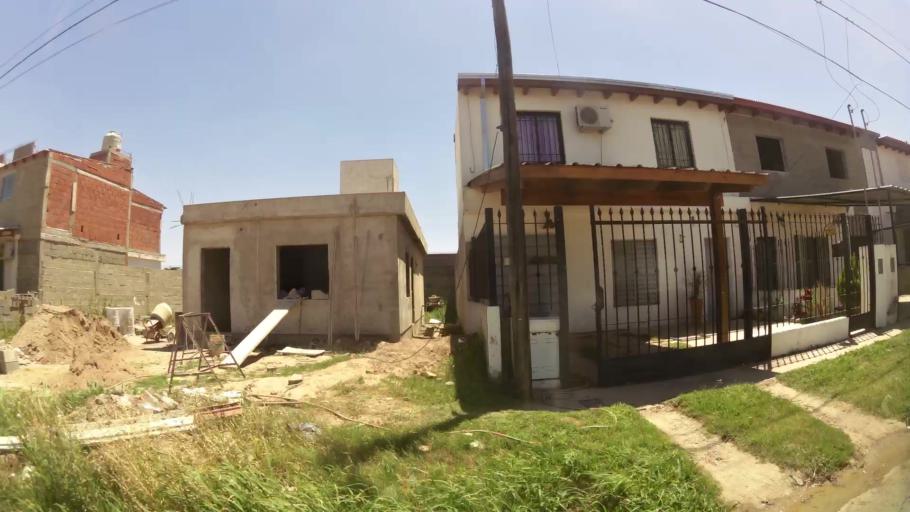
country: AR
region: Cordoba
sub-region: Departamento de Capital
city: Cordoba
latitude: -31.3870
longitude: -64.1417
